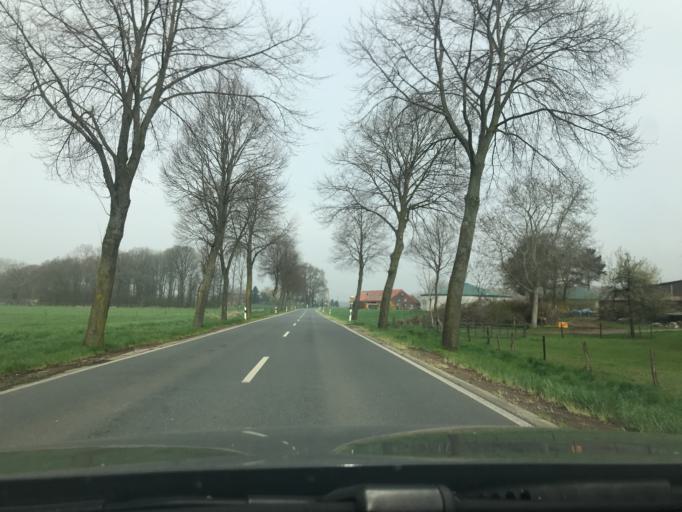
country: DE
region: North Rhine-Westphalia
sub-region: Regierungsbezirk Dusseldorf
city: Wachtendonk
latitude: 51.4282
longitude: 6.3480
